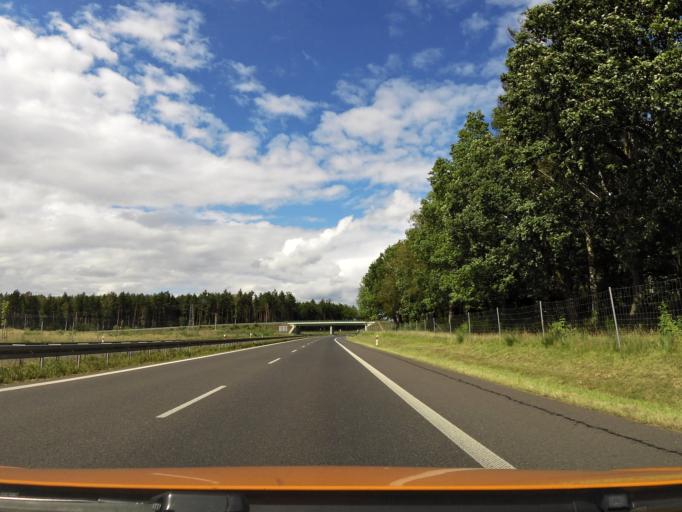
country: PL
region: West Pomeranian Voivodeship
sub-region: Powiat goleniowski
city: Nowogard
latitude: 53.6628
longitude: 15.0770
